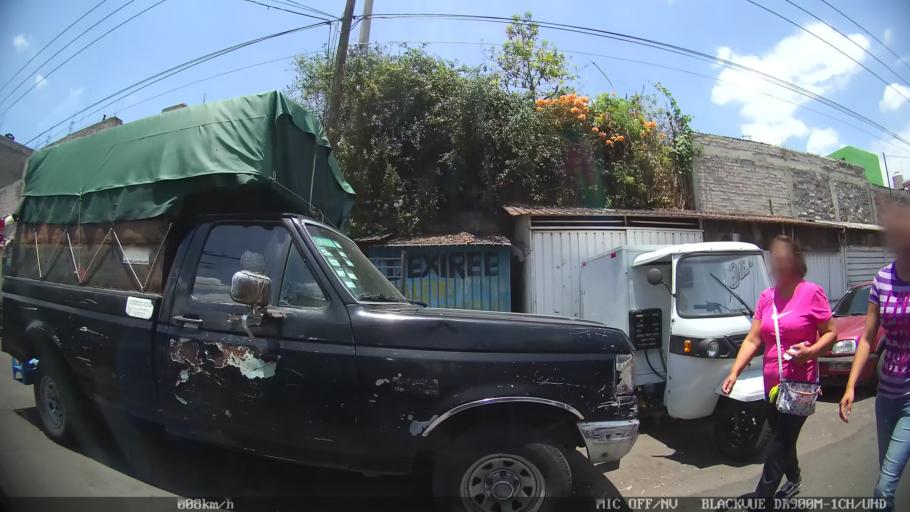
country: MX
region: Mexico City
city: Venustiano Carranza
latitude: 19.4273
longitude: -99.0586
